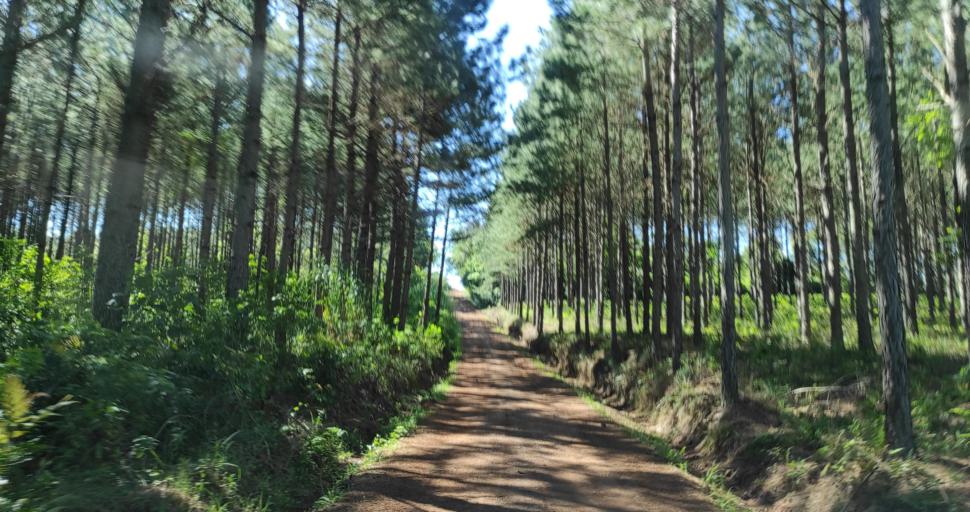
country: AR
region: Misiones
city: Capiovi
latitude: -26.9448
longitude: -55.0027
